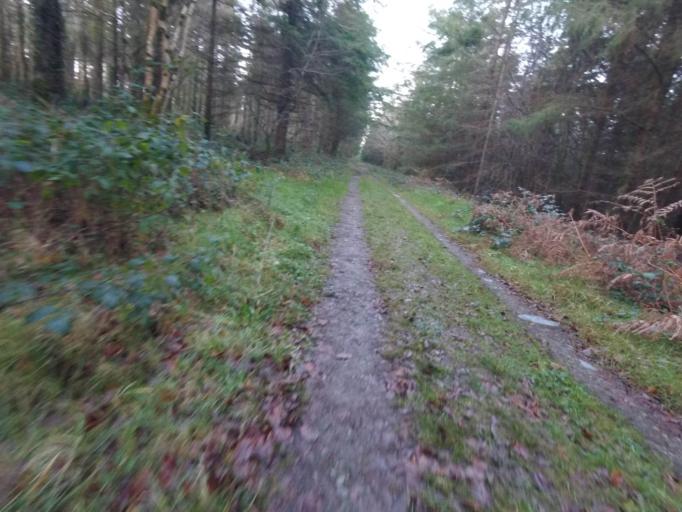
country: IE
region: Munster
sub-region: Waterford
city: Portlaw
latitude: 52.3018
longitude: -7.3427
